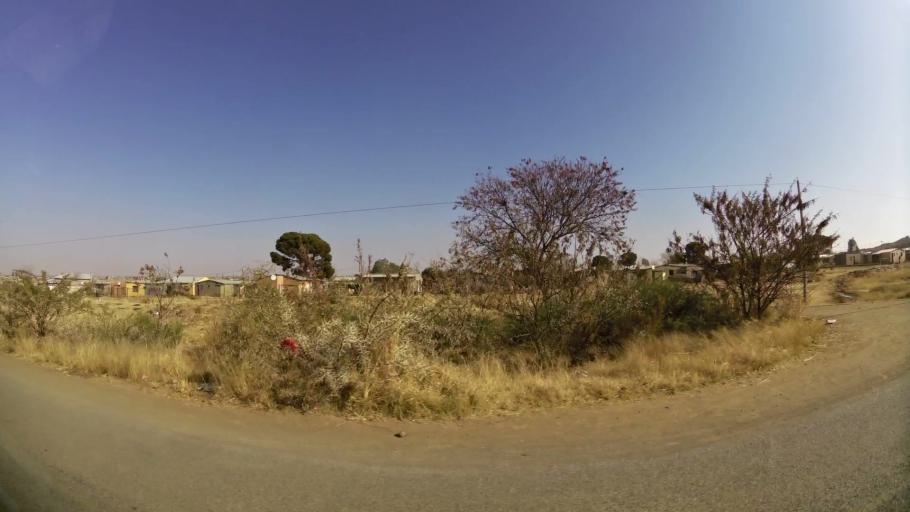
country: ZA
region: Orange Free State
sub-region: Mangaung Metropolitan Municipality
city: Bloemfontein
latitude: -29.1935
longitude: 26.2721
